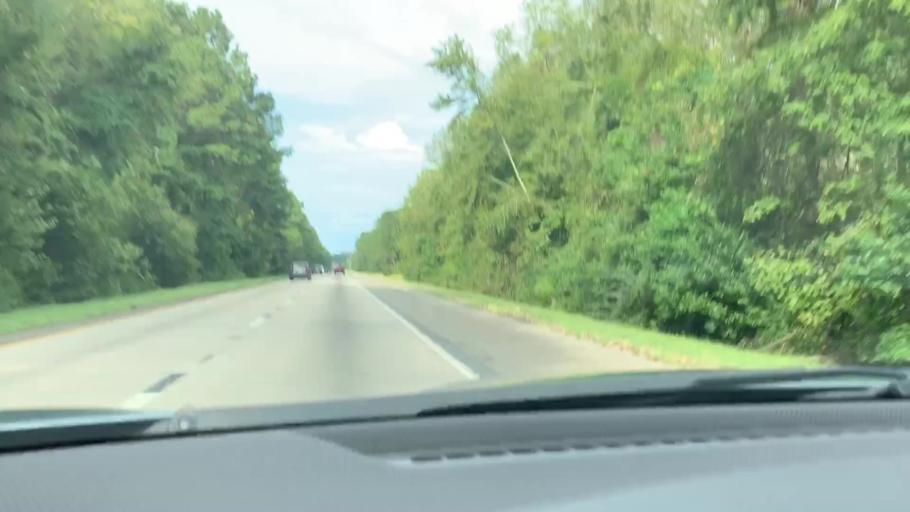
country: US
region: South Carolina
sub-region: Colleton County
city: Walterboro
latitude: 32.8961
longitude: -80.7087
